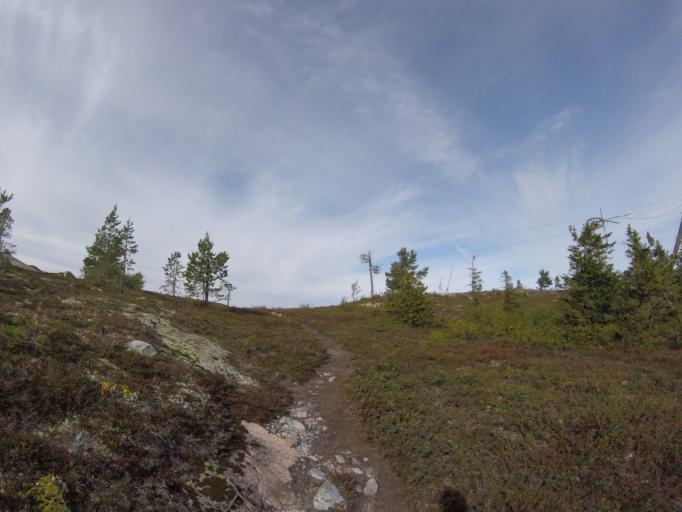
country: NO
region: Buskerud
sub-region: Flesberg
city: Lampeland
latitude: 59.7482
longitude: 9.4178
